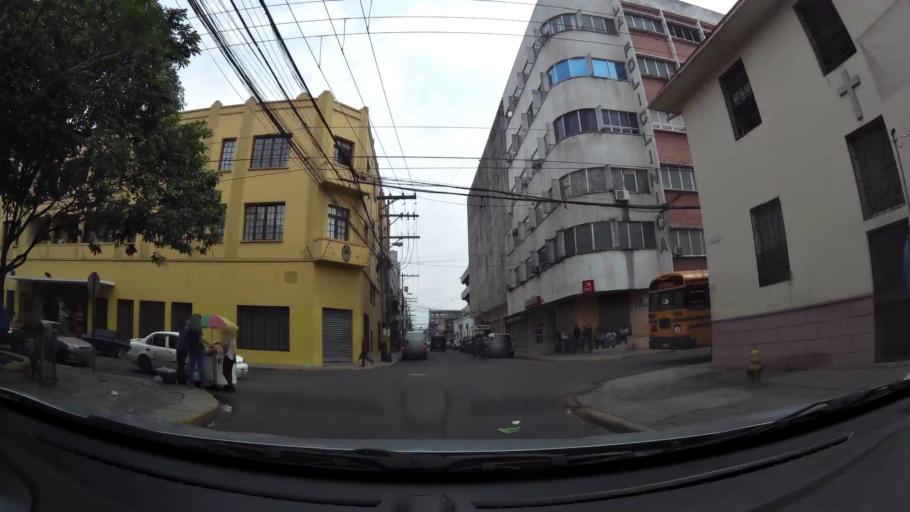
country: HN
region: Francisco Morazan
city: Tegucigalpa
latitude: 14.0981
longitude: -87.2074
